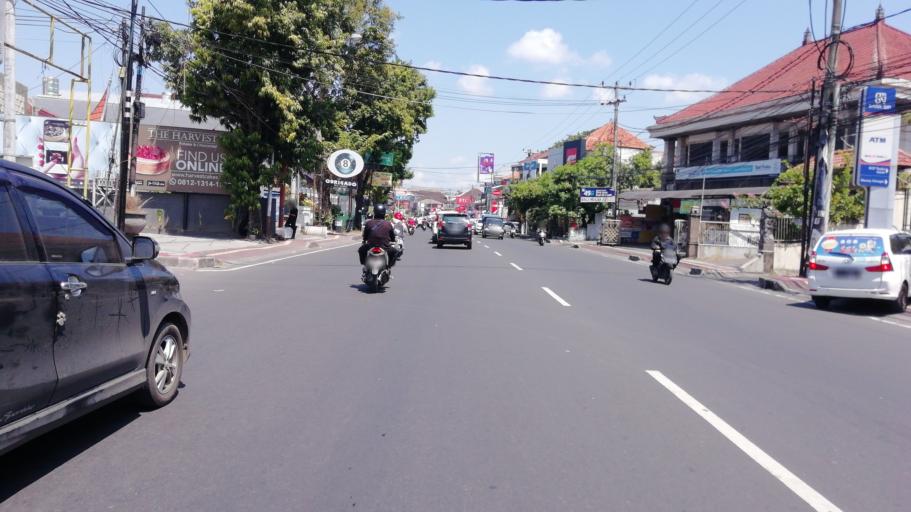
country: ID
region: Bali
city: Denpasar
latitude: -8.6720
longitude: 115.2089
